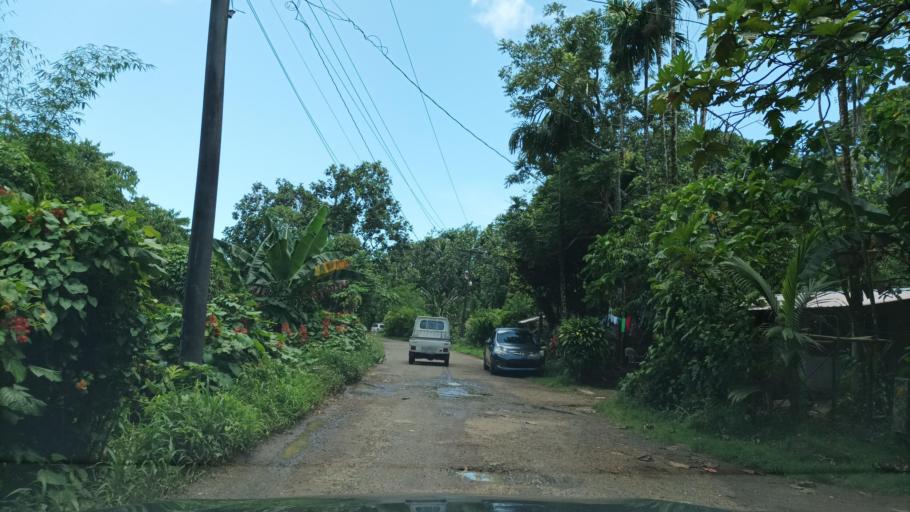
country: FM
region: Pohnpei
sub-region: Madolenihm Municipality
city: Madolenihm Municipality Government
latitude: 6.8440
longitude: 158.3050
